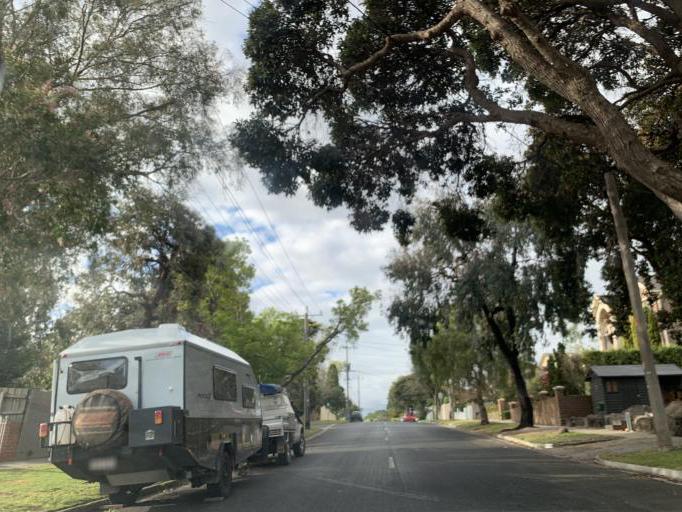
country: AU
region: Victoria
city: Beaumaris
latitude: -37.9796
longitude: 145.0390
